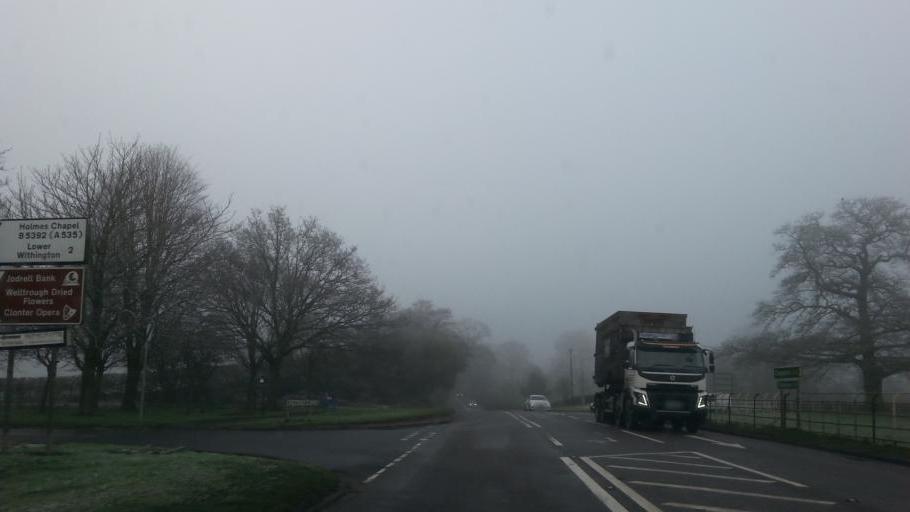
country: GB
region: England
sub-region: Cheshire East
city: Siddington
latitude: 53.2344
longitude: -2.2345
